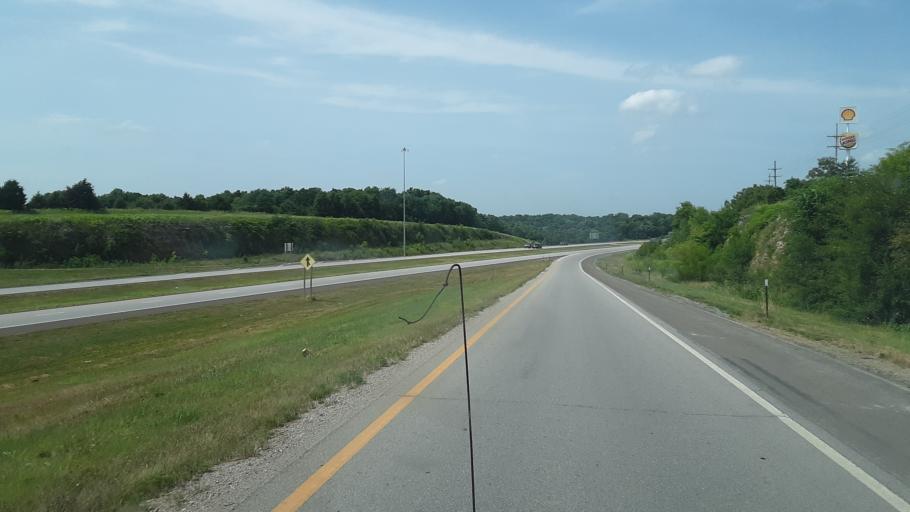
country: US
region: Kansas
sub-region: Miami County
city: Louisburg
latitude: 38.6218
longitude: -94.6944
